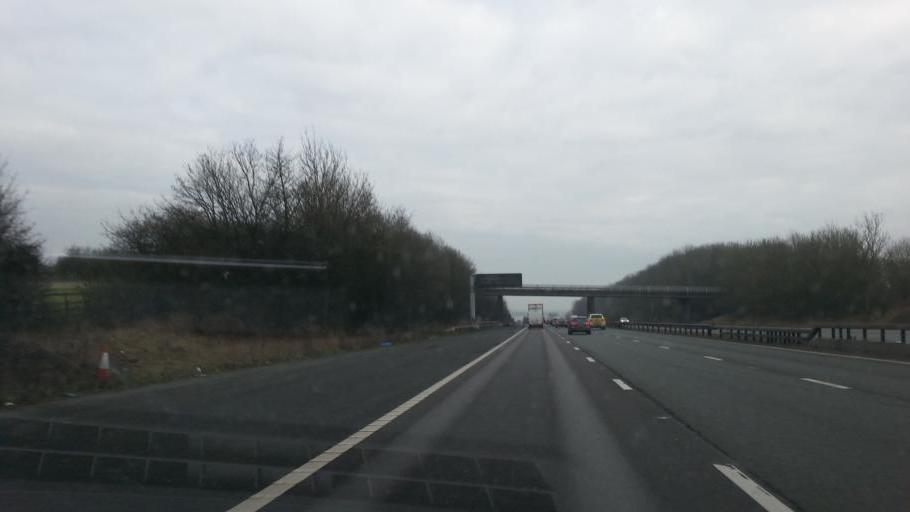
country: GB
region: England
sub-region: Warwickshire
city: Long Lawford
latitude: 52.4158
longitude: -1.2863
